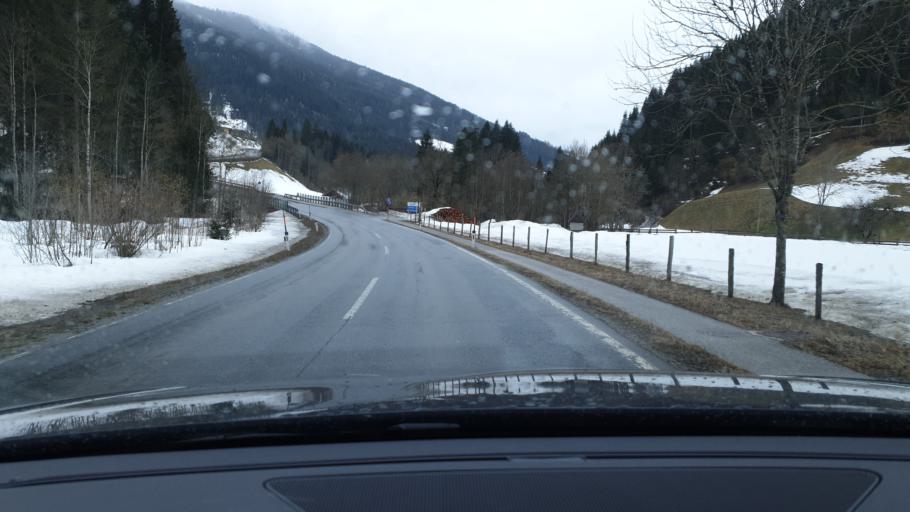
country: AT
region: Salzburg
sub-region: Politischer Bezirk Sankt Johann im Pongau
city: Eben im Pongau
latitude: 47.4199
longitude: 13.3997
